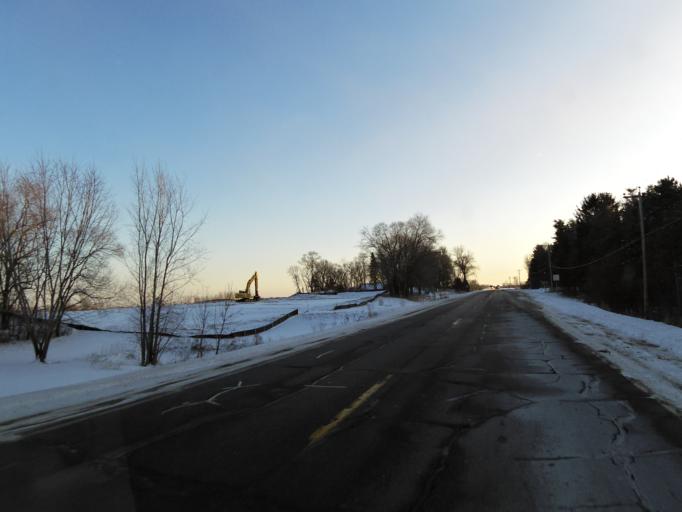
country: US
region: Minnesota
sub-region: Washington County
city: Lake Elmo
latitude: 44.9550
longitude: -92.8832
